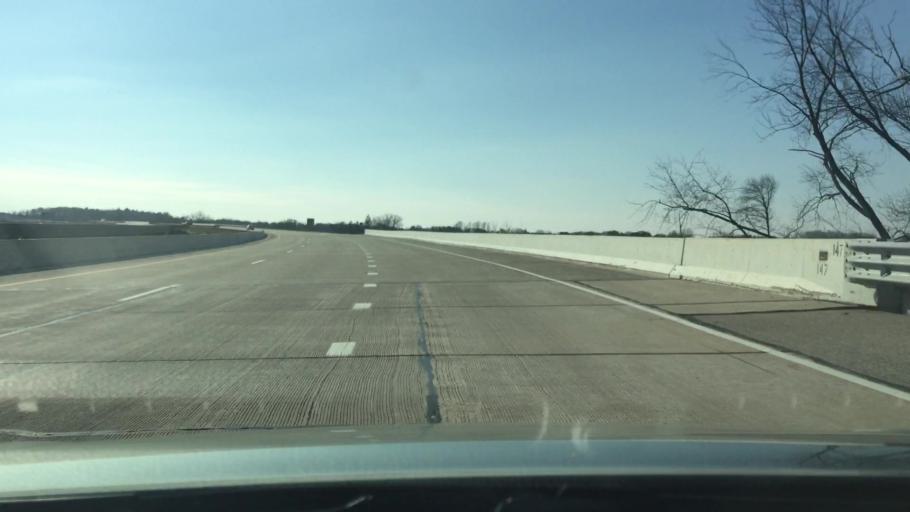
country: US
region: Wisconsin
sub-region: Jefferson County
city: Jefferson
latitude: 43.0098
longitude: -88.8327
